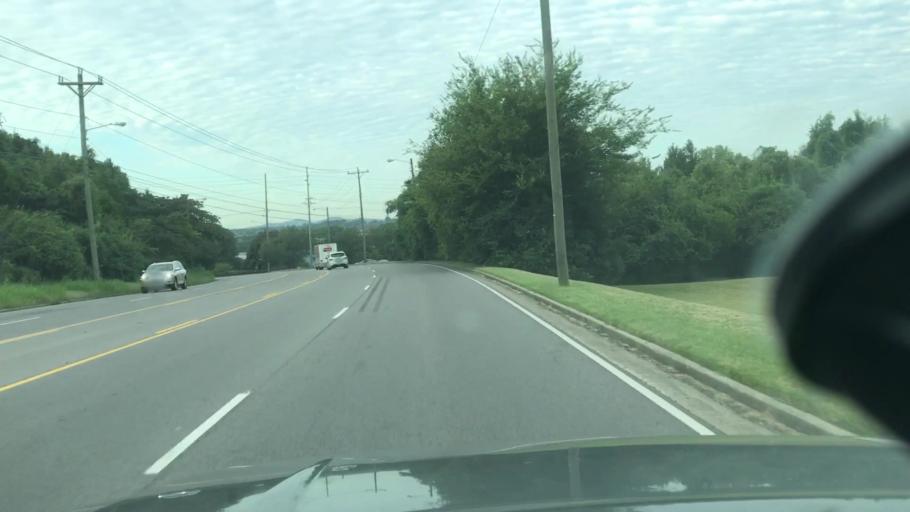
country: US
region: Tennessee
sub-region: Davidson County
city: Oak Hill
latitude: 36.1000
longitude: -86.6765
